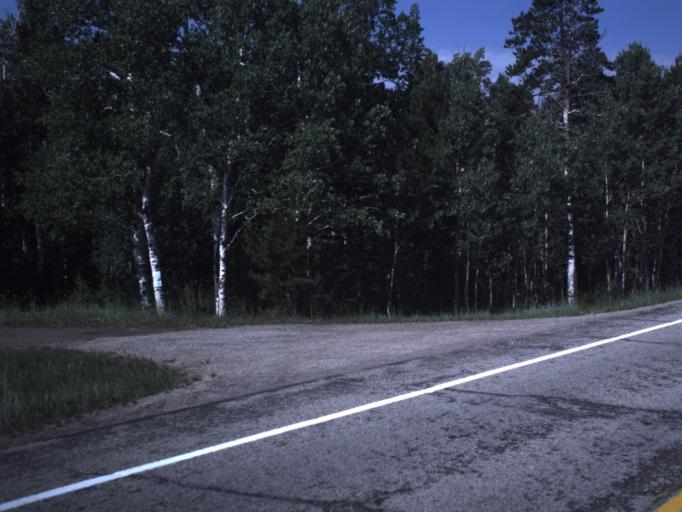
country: US
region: Utah
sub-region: Daggett County
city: Manila
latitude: 40.8496
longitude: -109.5861
